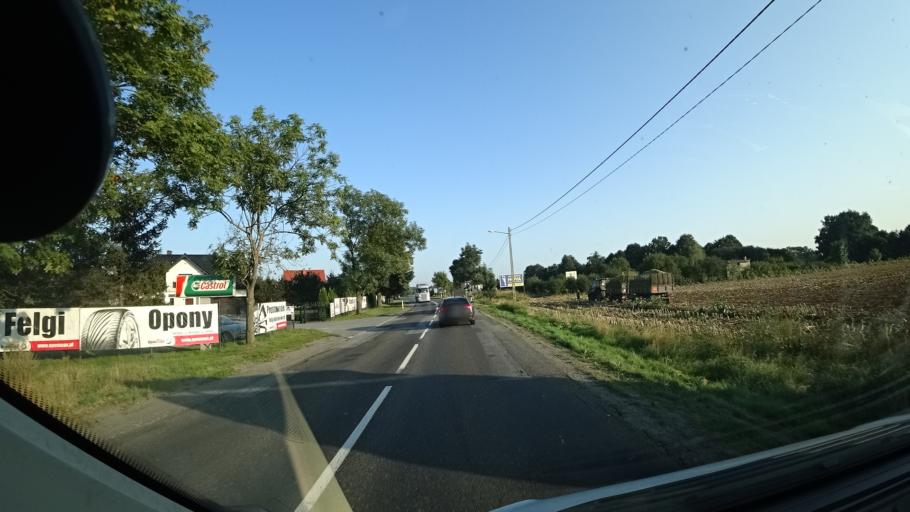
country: PL
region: Opole Voivodeship
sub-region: Powiat kedzierzynsko-kozielski
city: Kedzierzyn-Kozle
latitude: 50.3279
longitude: 18.2008
